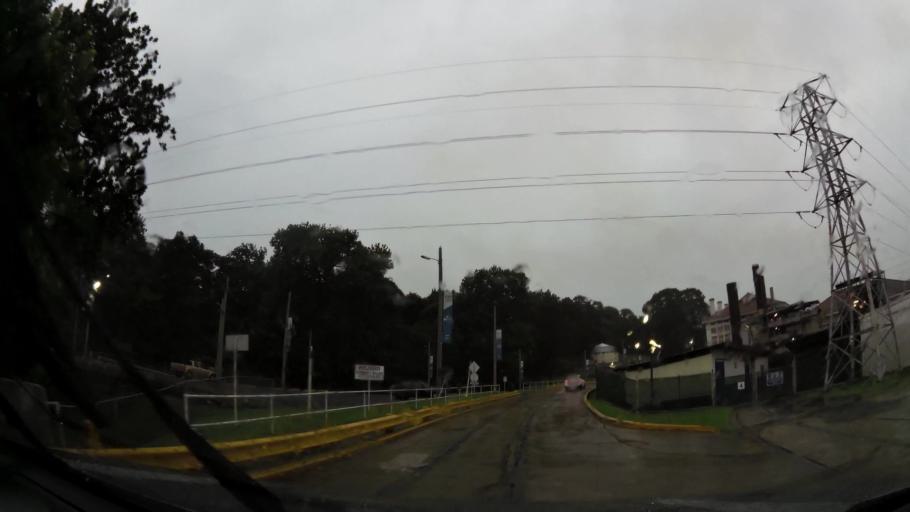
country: PA
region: Panama
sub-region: Distrito de Panama
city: Paraiso
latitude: 9.0008
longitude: -79.5919
